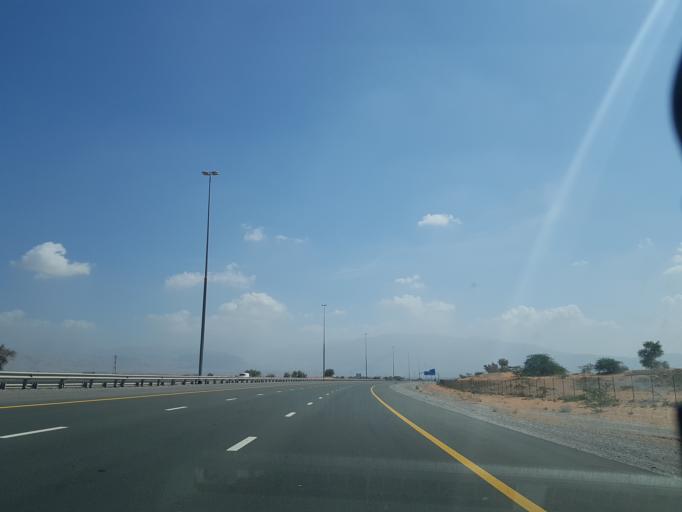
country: AE
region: Ra's al Khaymah
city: Ras al-Khaimah
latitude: 25.7058
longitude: 55.9461
